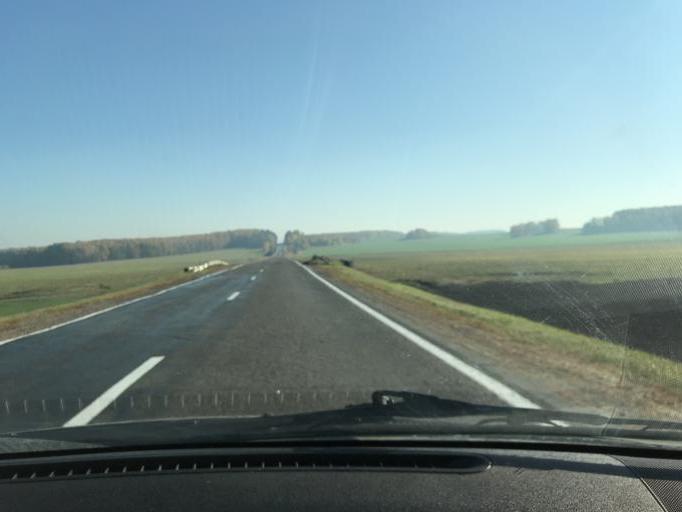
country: BY
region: Minsk
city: Klyetsk
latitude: 52.9683
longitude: 26.5991
